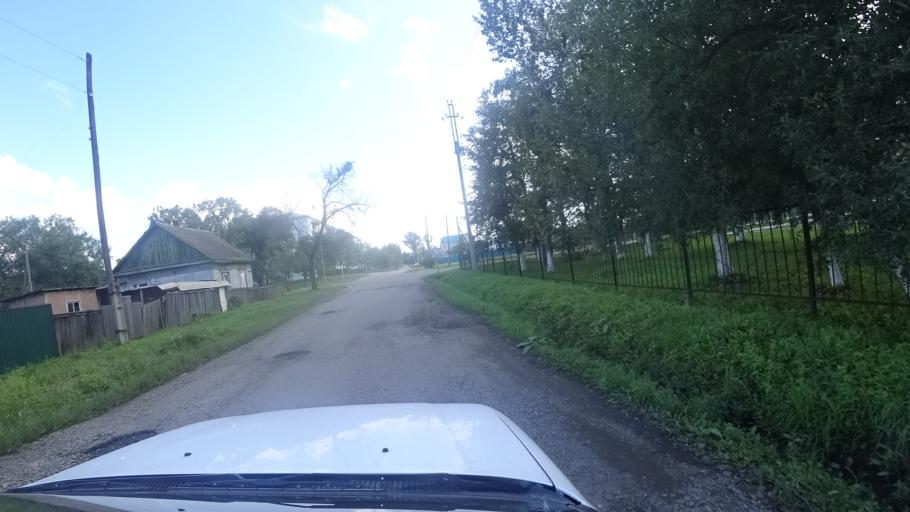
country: RU
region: Primorskiy
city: Dal'nerechensk
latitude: 45.9359
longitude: 133.7398
